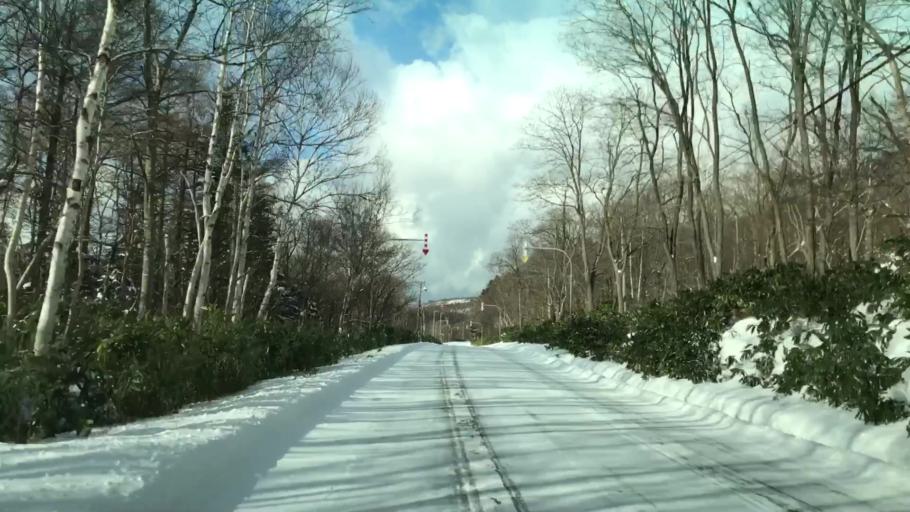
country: JP
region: Hokkaido
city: Yoichi
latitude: 43.3202
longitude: 140.5212
